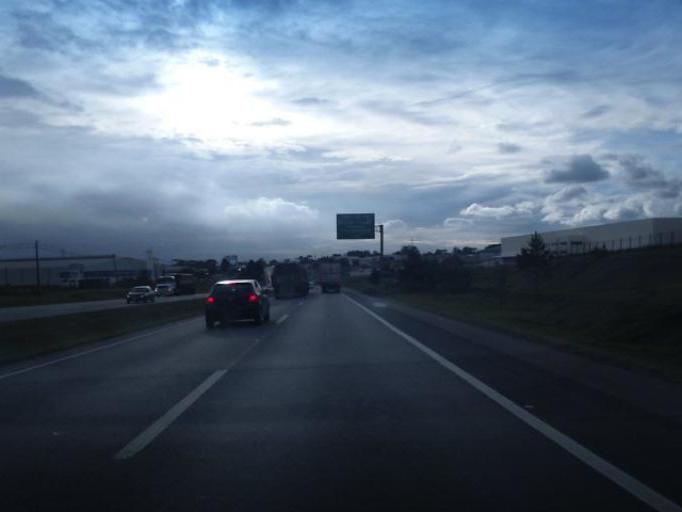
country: BR
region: Parana
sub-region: Sao Jose Dos Pinhais
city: Sao Jose dos Pinhais
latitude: -25.5656
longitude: -49.1644
